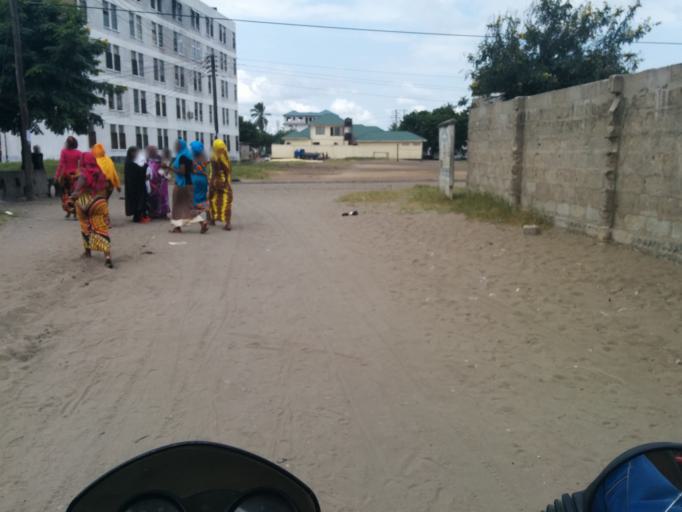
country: TZ
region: Dar es Salaam
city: Dar es Salaam
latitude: -6.8619
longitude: 39.2563
